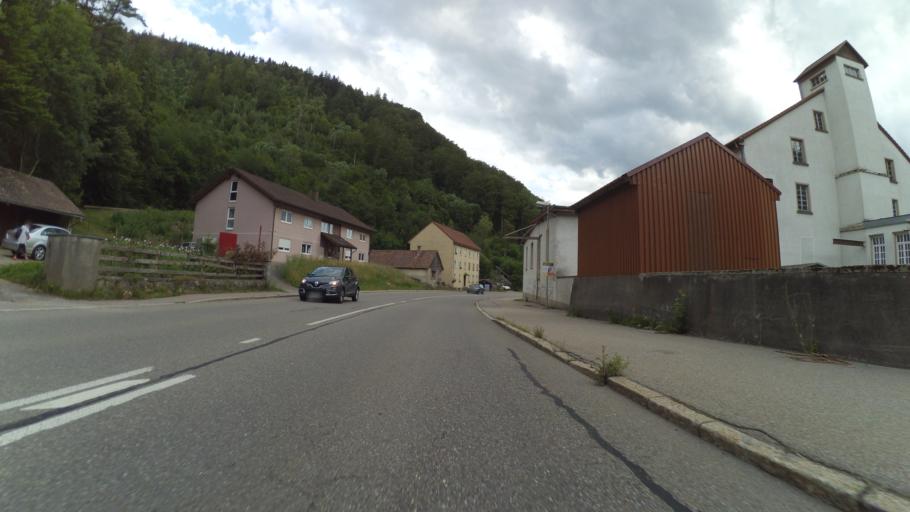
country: DE
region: Baden-Wuerttemberg
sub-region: Freiburg Region
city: Todtnau
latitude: 47.8249
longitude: 7.9411
